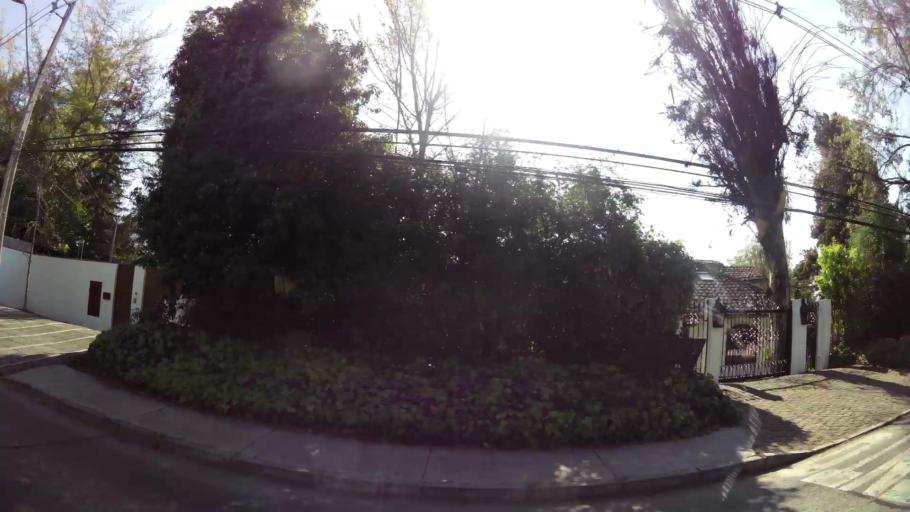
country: CL
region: Santiago Metropolitan
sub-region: Provincia de Santiago
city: Villa Presidente Frei, Nunoa, Santiago, Chile
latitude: -33.3891
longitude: -70.5199
